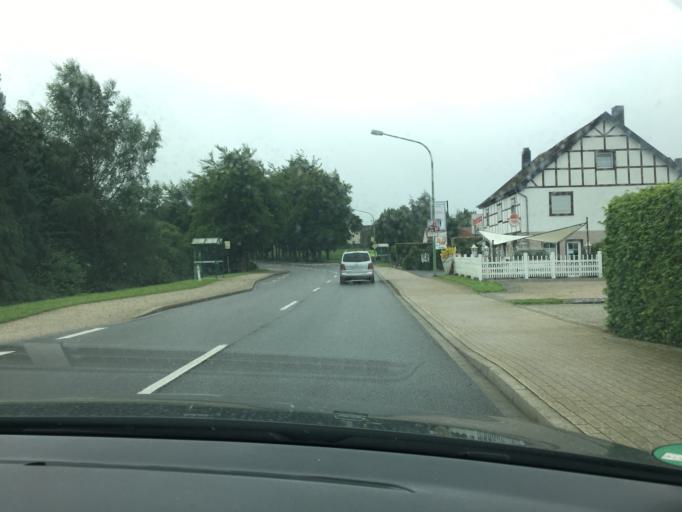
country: DE
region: North Rhine-Westphalia
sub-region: Regierungsbezirk Koln
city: Hurtgenwald
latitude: 50.6828
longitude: 6.3475
